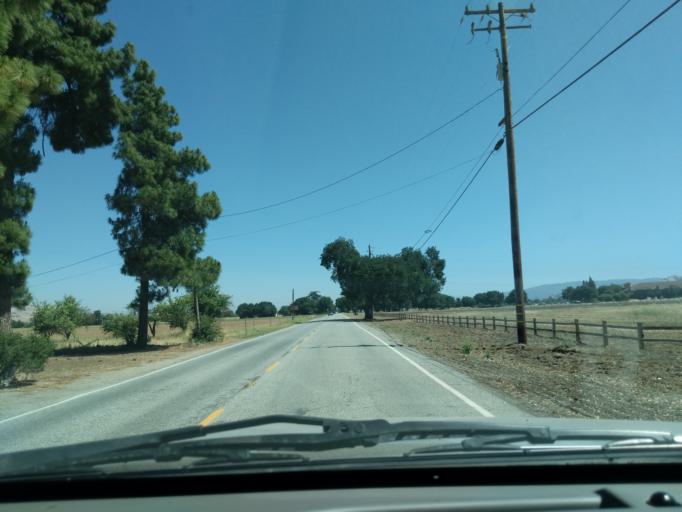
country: US
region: California
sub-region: Santa Clara County
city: Morgan Hill
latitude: 37.1249
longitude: -121.6234
